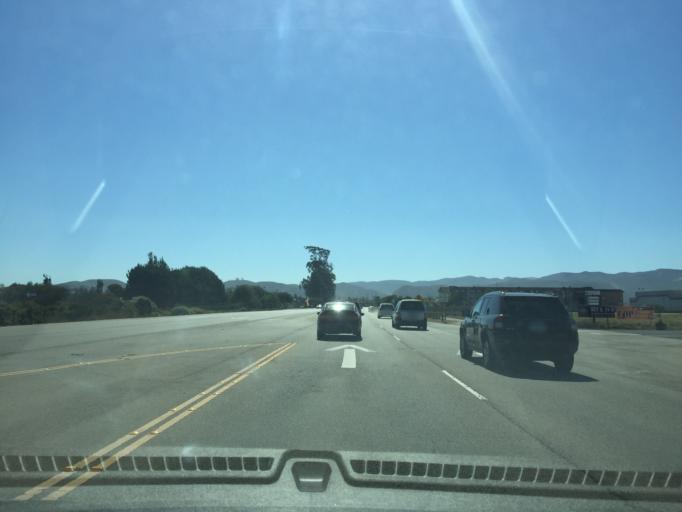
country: US
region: California
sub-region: Santa Barbara County
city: Lompoc
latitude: 34.6668
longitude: -120.4577
